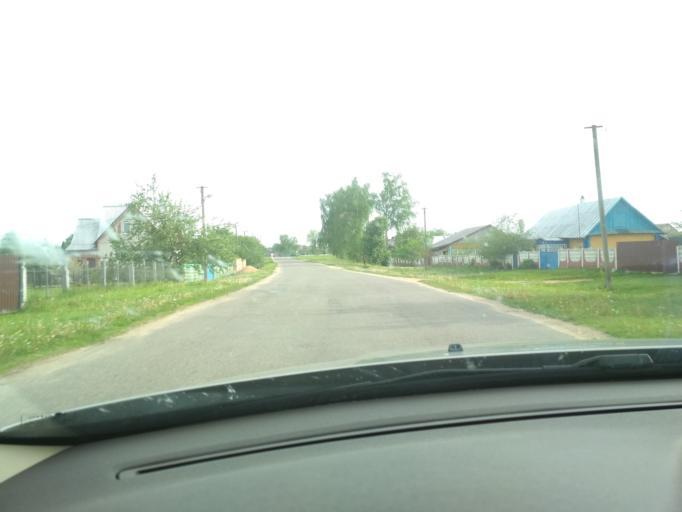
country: BY
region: Grodnenskaya
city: Mir
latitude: 53.4256
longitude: 26.4418
